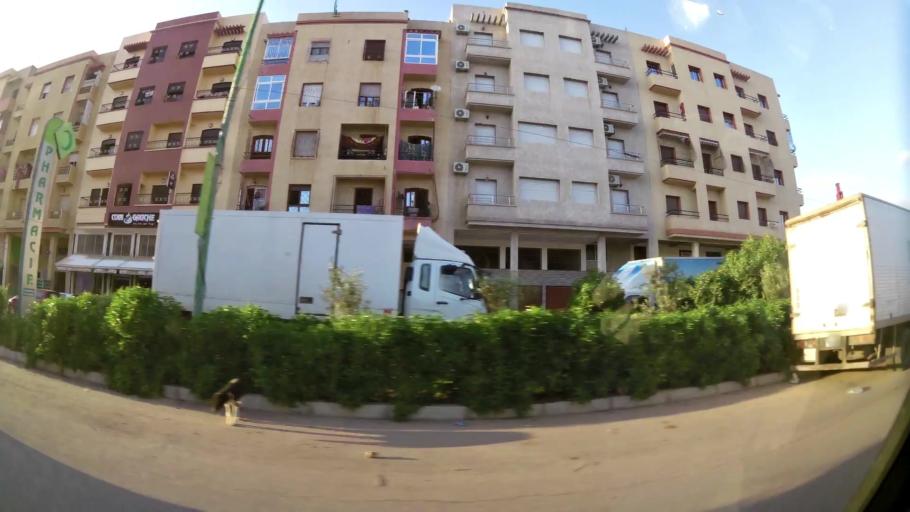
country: MA
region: Chaouia-Ouardigha
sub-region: Settat Province
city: Settat
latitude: 32.9913
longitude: -7.6018
